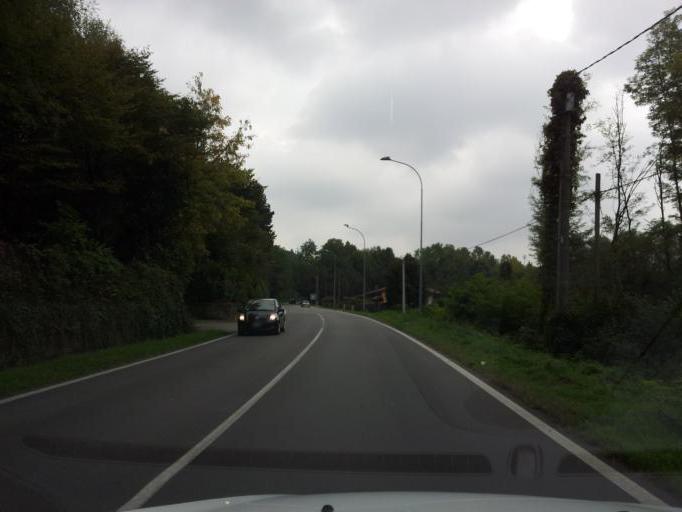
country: IT
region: Lombardy
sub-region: Provincia di Varese
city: Corgeno
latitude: 45.7546
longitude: 8.6976
